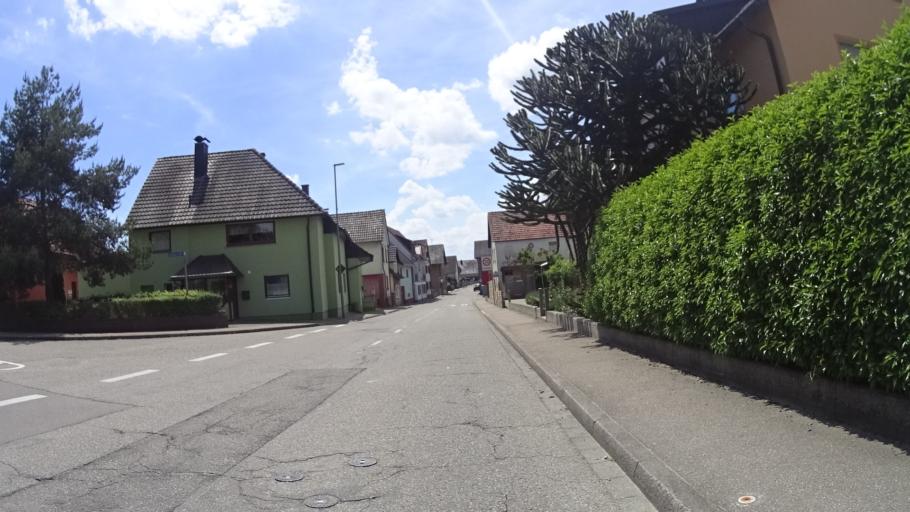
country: DE
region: Baden-Wuerttemberg
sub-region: Freiburg Region
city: Rust
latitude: 48.2729
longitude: 7.7311
